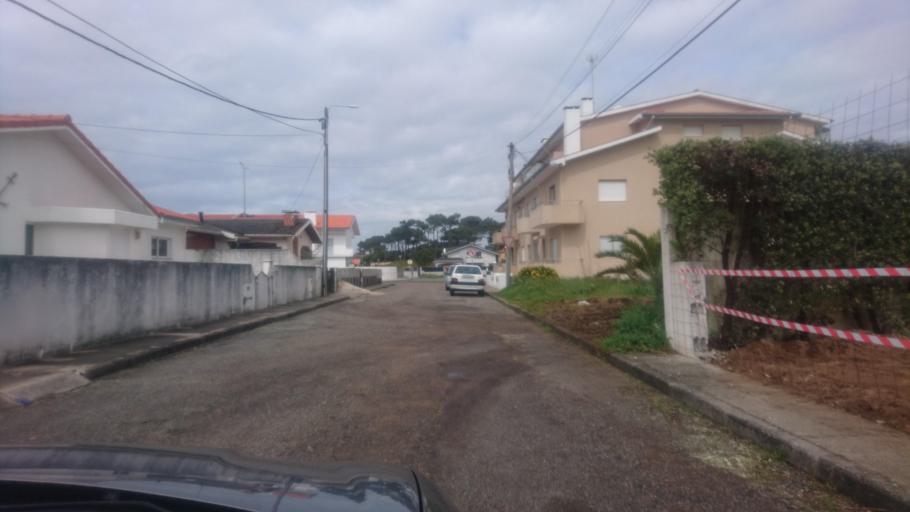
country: PT
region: Aveiro
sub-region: Ovar
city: Esmoriz
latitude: 40.9559
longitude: -8.6496
